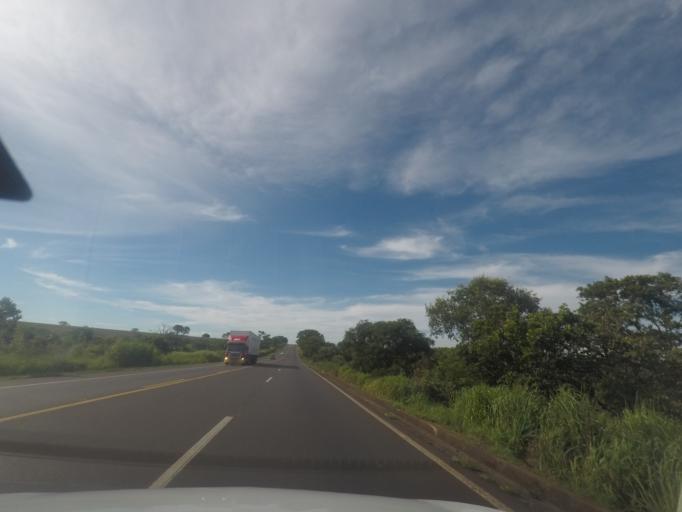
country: BR
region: Minas Gerais
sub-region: Monte Alegre De Minas
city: Monte Alegre de Minas
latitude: -18.9229
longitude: -49.0334
